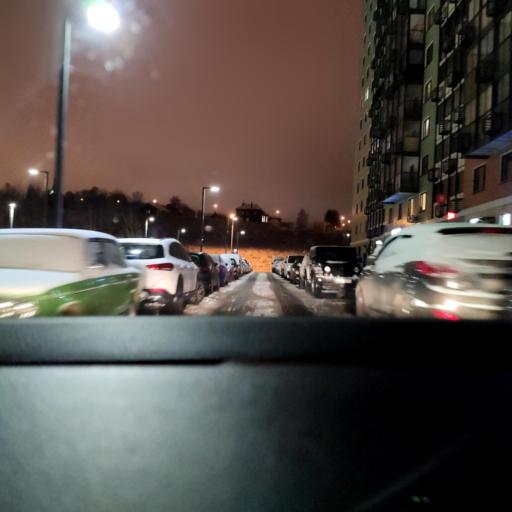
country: RU
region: Moskovskaya
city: Pavshino
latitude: 55.8621
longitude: 37.3734
